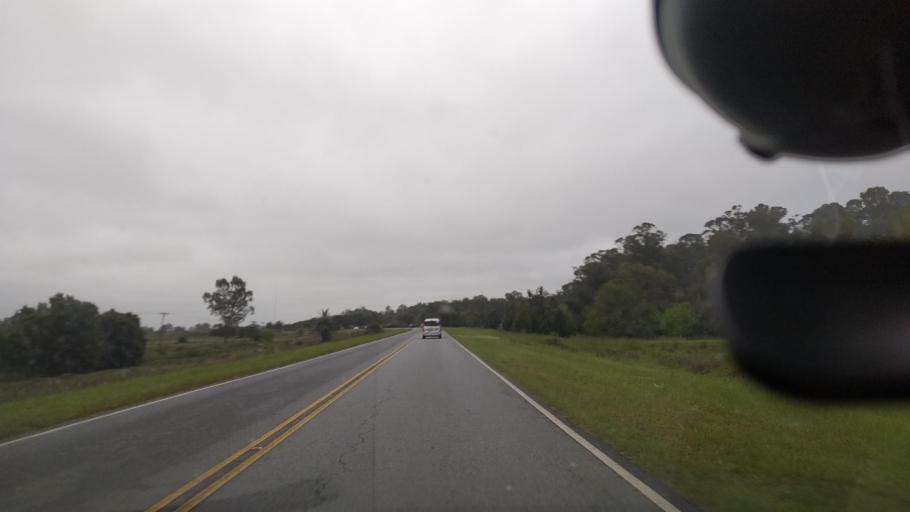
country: AR
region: Buenos Aires
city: Veronica
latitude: -35.4129
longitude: -57.3465
